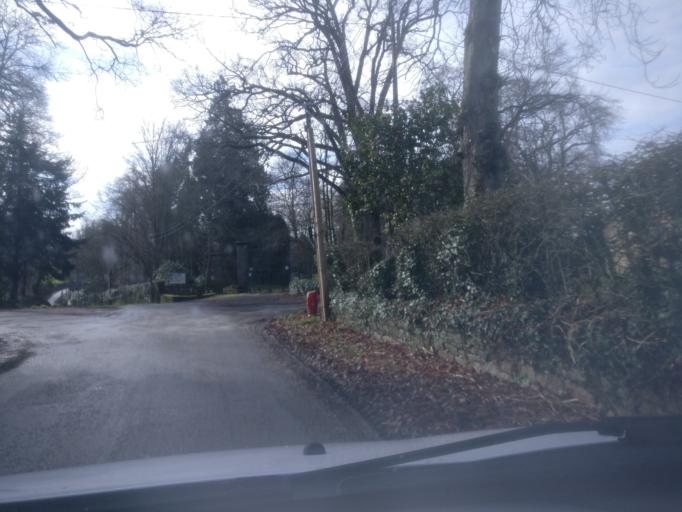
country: FR
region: Brittany
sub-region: Departement d'Ille-et-Vilaine
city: Antrain
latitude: 48.4494
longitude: -1.4864
